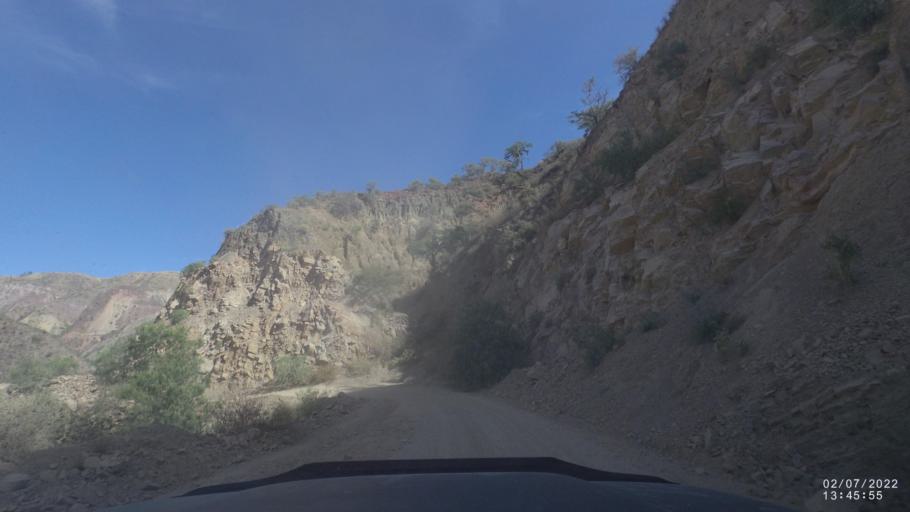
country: BO
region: Cochabamba
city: Irpa Irpa
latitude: -17.8112
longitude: -66.3655
